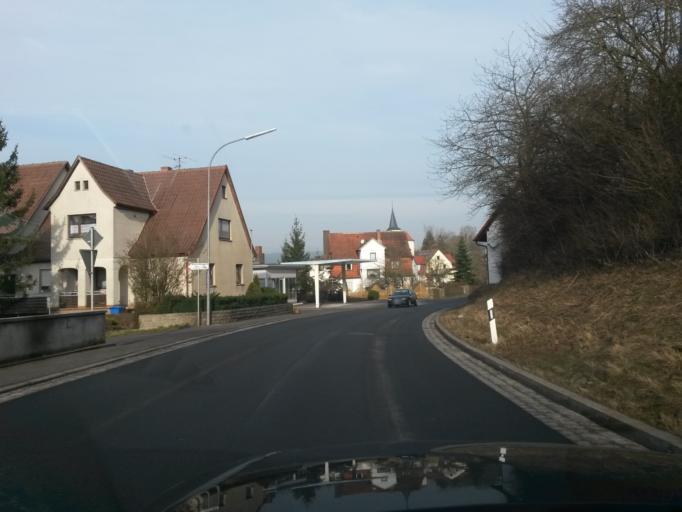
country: DE
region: Bavaria
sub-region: Regierungsbezirk Unterfranken
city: Sondheim vor der Rhoen
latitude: 50.4769
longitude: 10.1885
